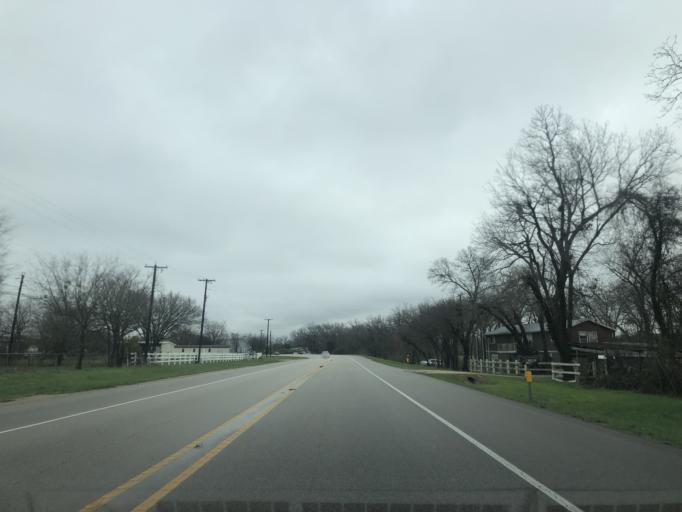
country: US
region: Texas
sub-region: Williamson County
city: Georgetown
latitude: 30.6419
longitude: -97.5756
